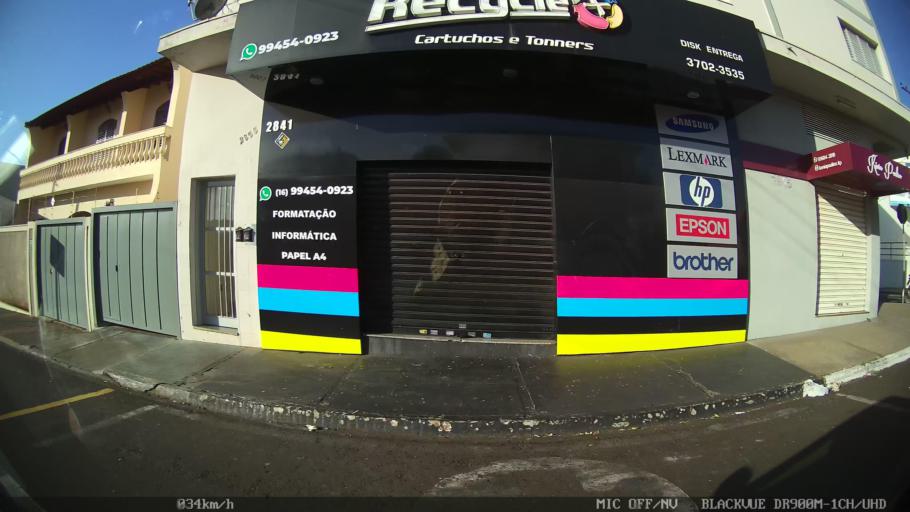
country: BR
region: Sao Paulo
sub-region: Franca
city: Franca
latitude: -20.5409
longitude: -47.3877
